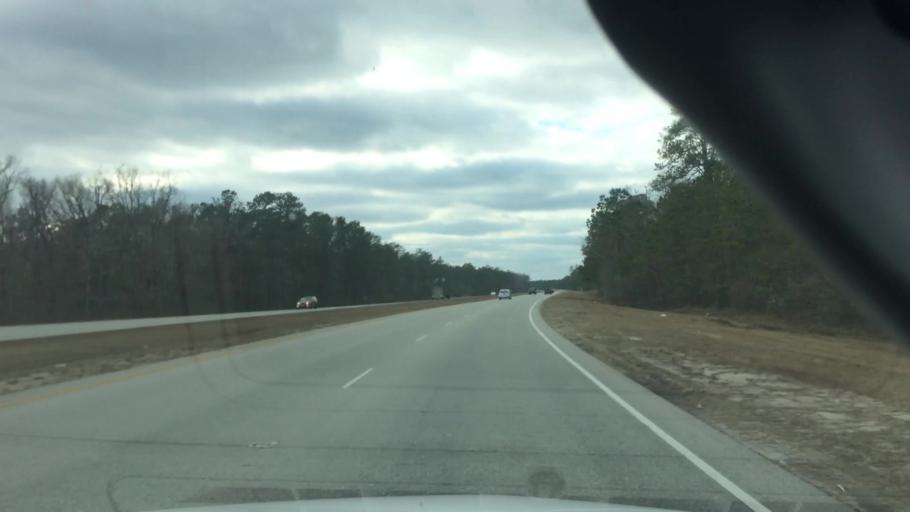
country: US
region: North Carolina
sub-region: Brunswick County
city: Bolivia
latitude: 34.0782
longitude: -78.1447
